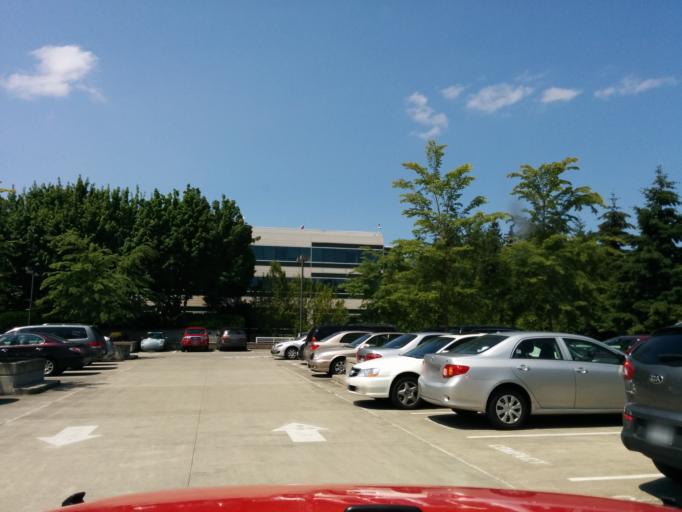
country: US
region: Washington
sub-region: King County
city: Redmond
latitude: 47.6455
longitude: -122.1291
